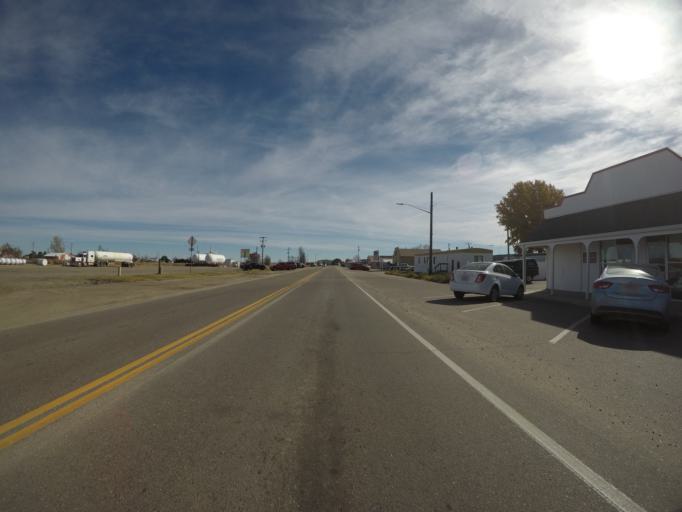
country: US
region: Colorado
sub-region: Adams County
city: Bennett
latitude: 39.7558
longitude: -104.4269
